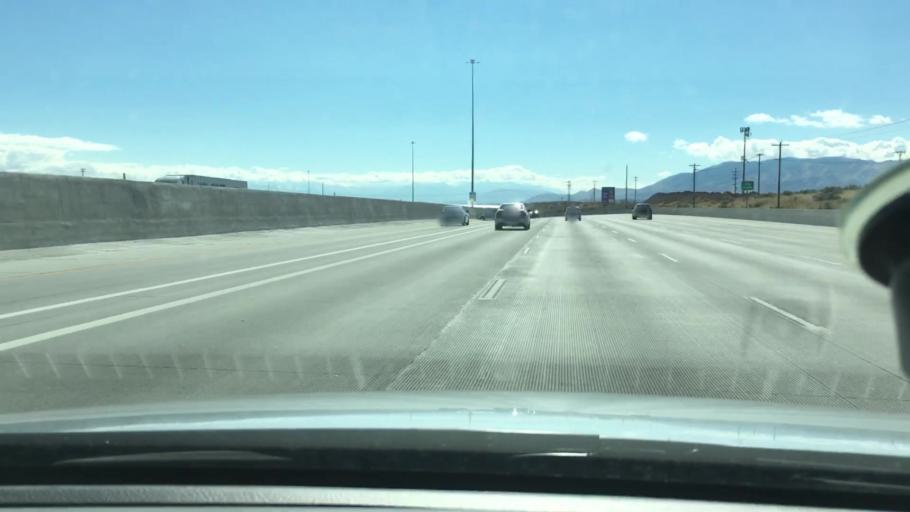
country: US
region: Utah
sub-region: Salt Lake County
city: Bluffdale
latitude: 40.4531
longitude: -111.9138
